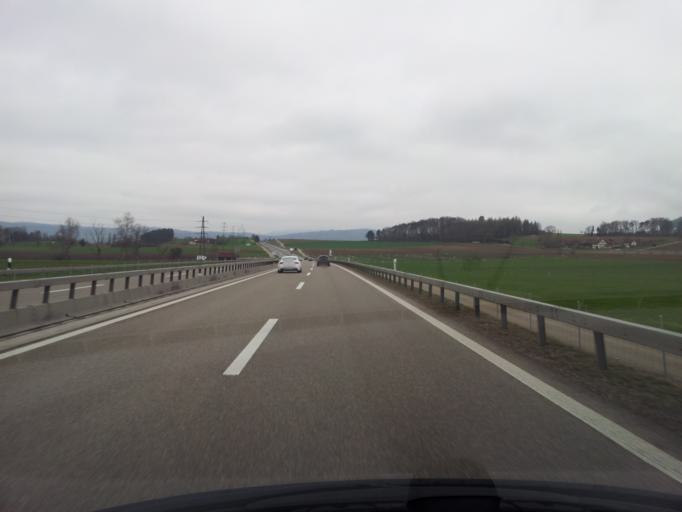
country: CH
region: Zurich
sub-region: Bezirk Andelfingen
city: Uhwiesen
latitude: 47.6529
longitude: 8.6427
